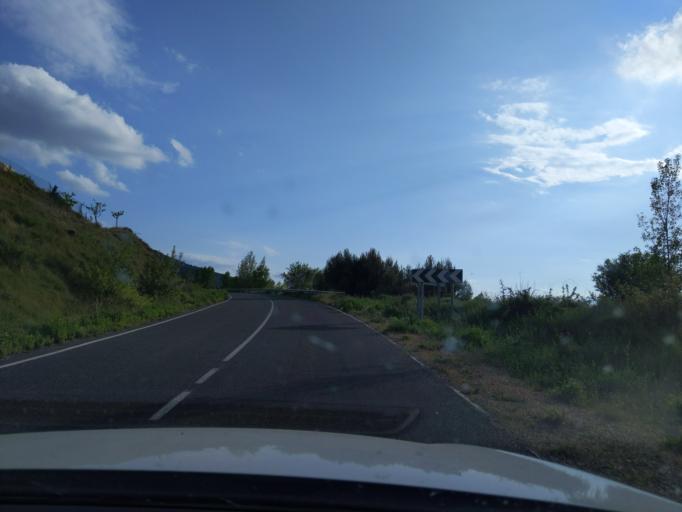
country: ES
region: La Rioja
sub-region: Provincia de La Rioja
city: Clavijo
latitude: 42.3627
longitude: -2.4243
